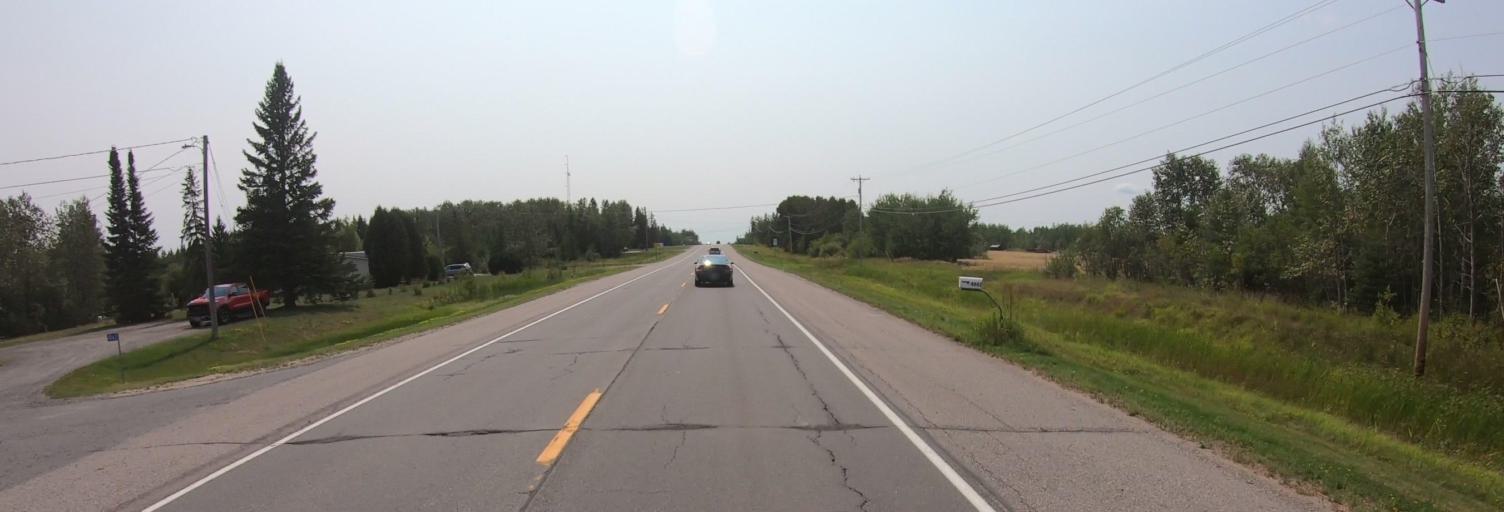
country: US
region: Minnesota
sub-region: Koochiching County
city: International Falls
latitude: 48.5731
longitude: -93.4399
